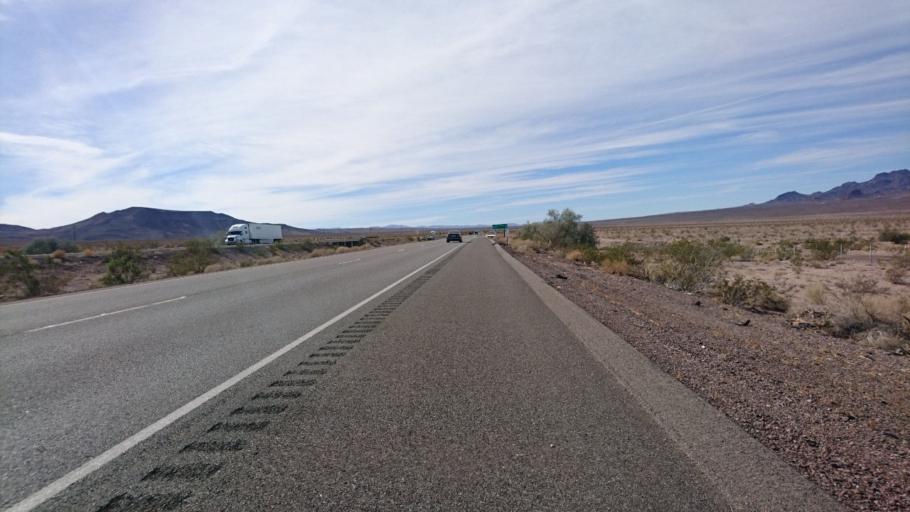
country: US
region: California
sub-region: San Bernardino County
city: Twentynine Palms
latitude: 34.7250
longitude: -116.1779
